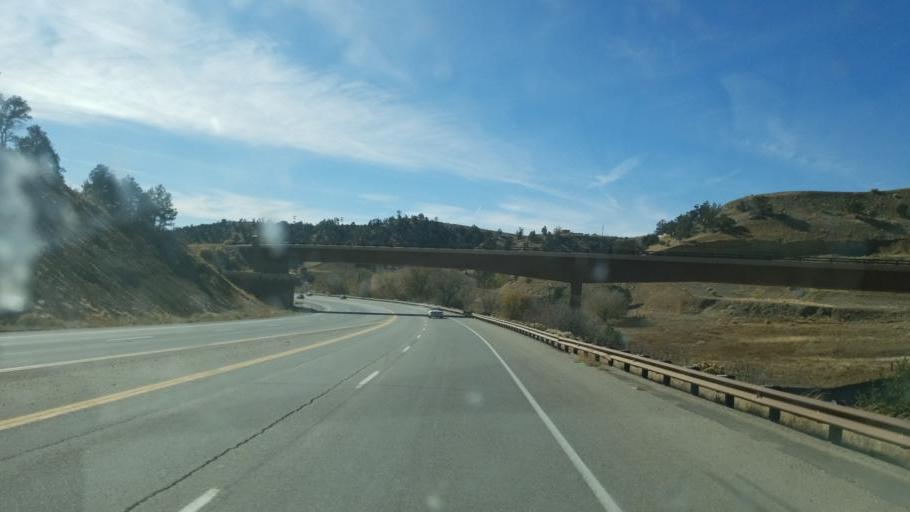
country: US
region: Colorado
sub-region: La Plata County
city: Durango
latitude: 37.2275
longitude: -107.8398
